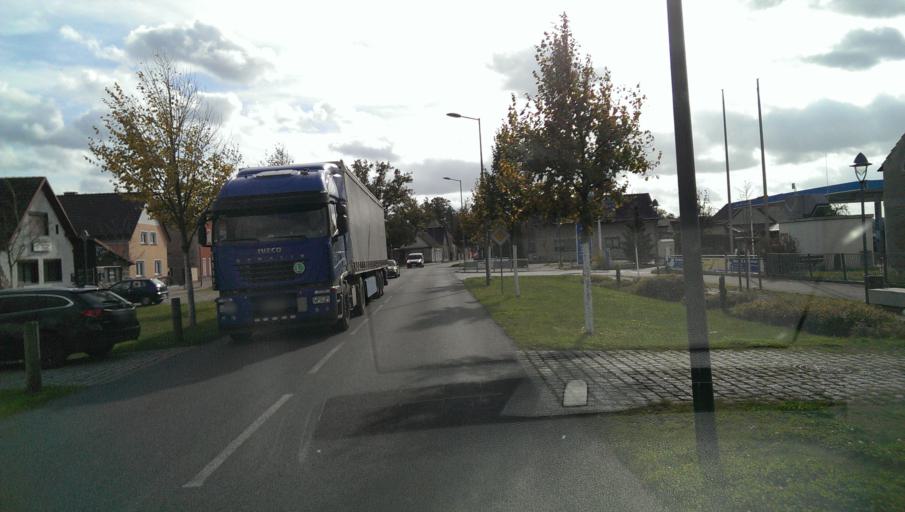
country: DE
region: Brandenburg
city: Lauchhammer
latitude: 51.4691
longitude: 13.7396
